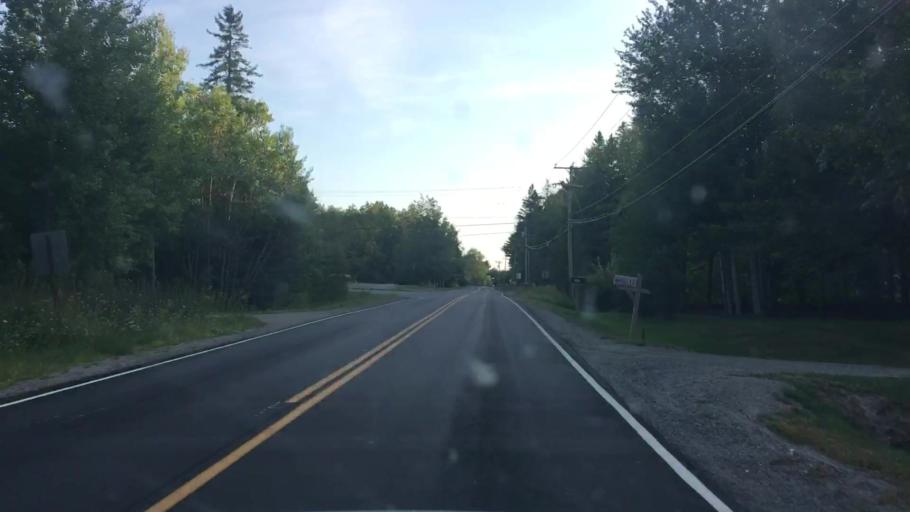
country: US
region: Maine
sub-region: Penobscot County
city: Hampden
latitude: 44.7201
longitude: -68.8863
